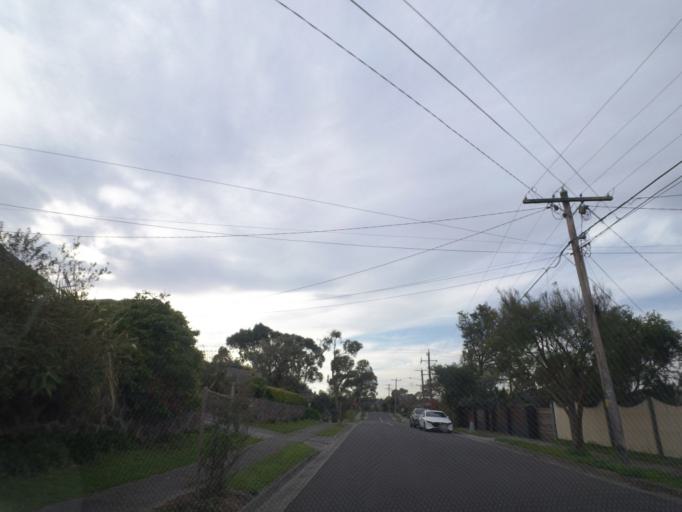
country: AU
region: Victoria
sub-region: Knox
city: Ferntree Gully
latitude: -37.8963
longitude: 145.2922
